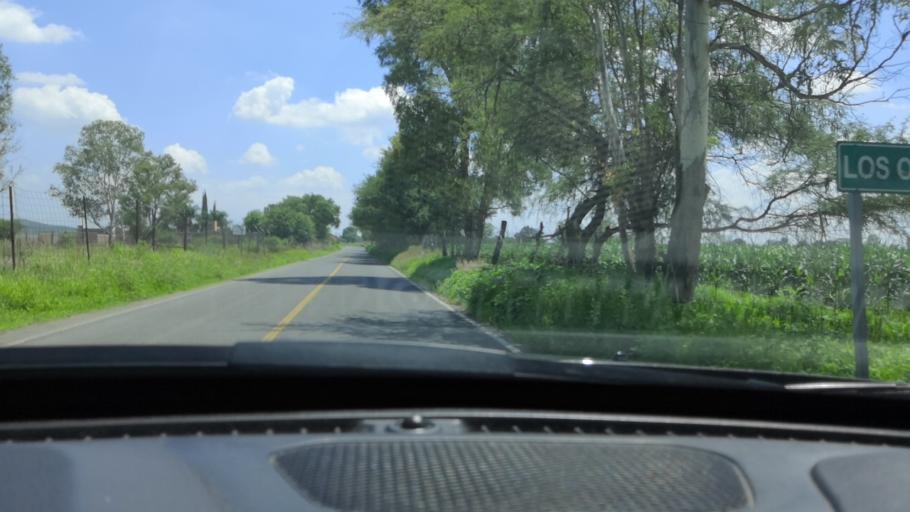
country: MX
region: Guanajuato
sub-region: Silao de la Victoria
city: El Refugio de los Sauces
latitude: 20.9599
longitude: -101.5891
